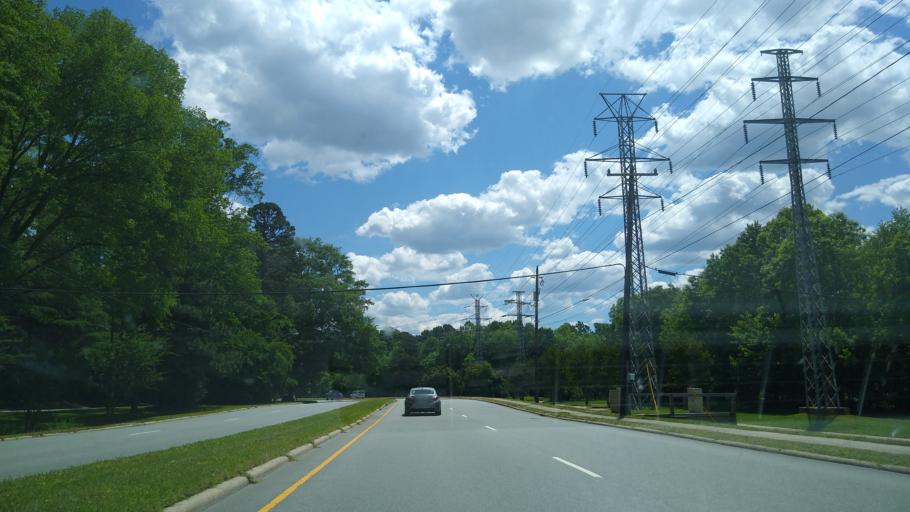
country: US
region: North Carolina
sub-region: Guilford County
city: Greensboro
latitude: 36.0794
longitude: -79.8109
